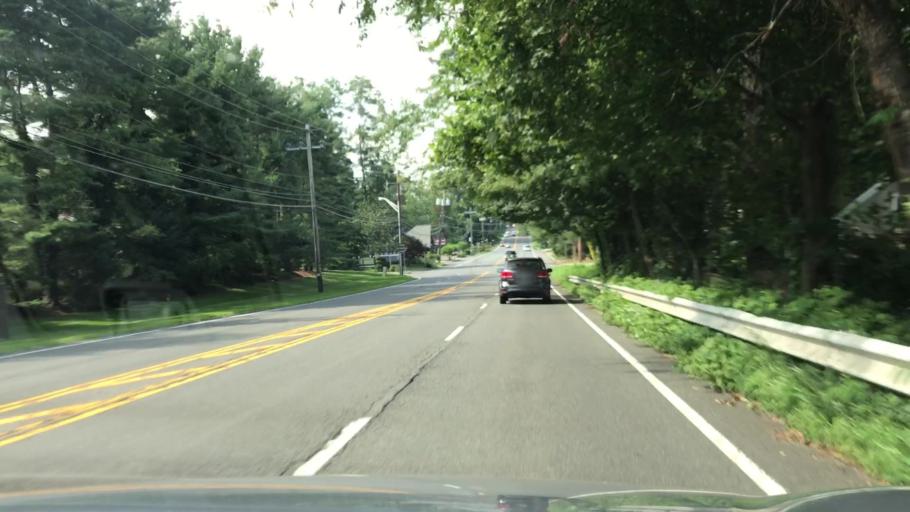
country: US
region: New York
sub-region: Rockland County
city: Tappan
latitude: 41.0228
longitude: -73.9426
